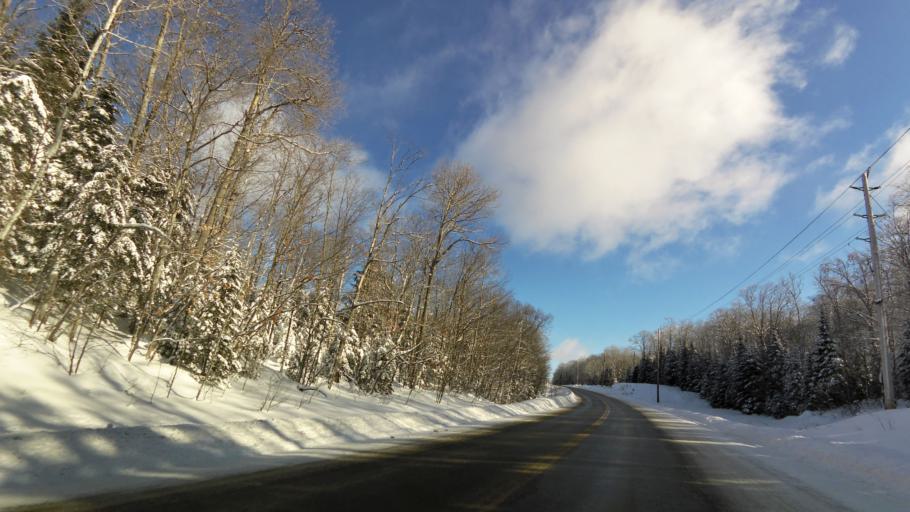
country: CA
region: Ontario
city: Bancroft
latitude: 45.0117
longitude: -78.3405
